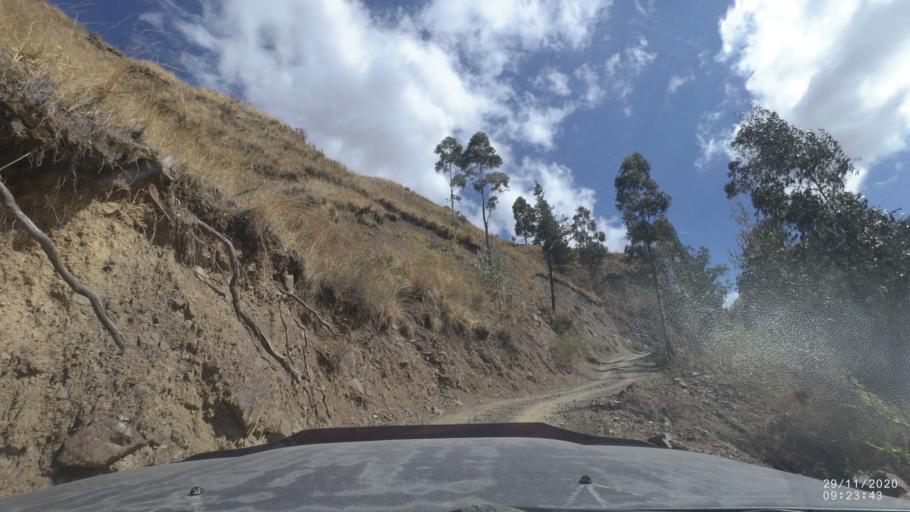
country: BO
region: Cochabamba
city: Cochabamba
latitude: -17.3207
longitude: -66.1856
